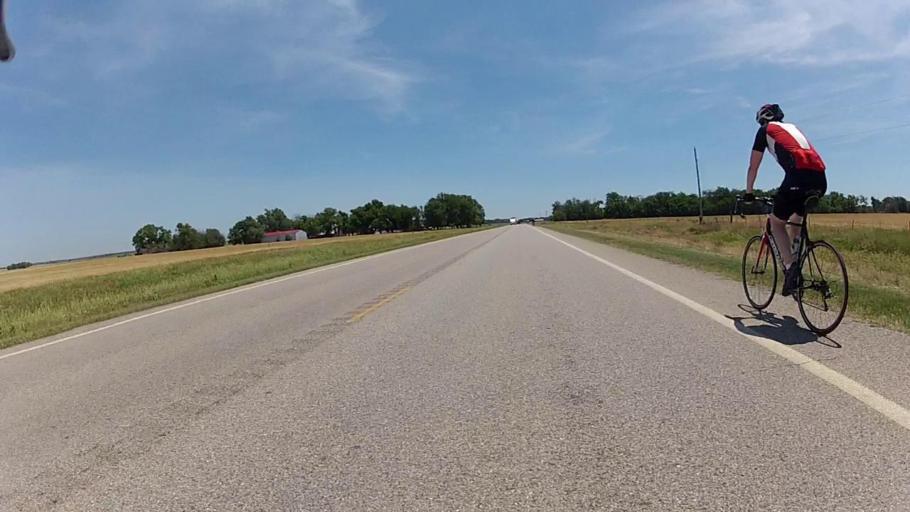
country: US
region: Kansas
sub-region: Barber County
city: Medicine Lodge
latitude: 37.2534
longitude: -98.4356
